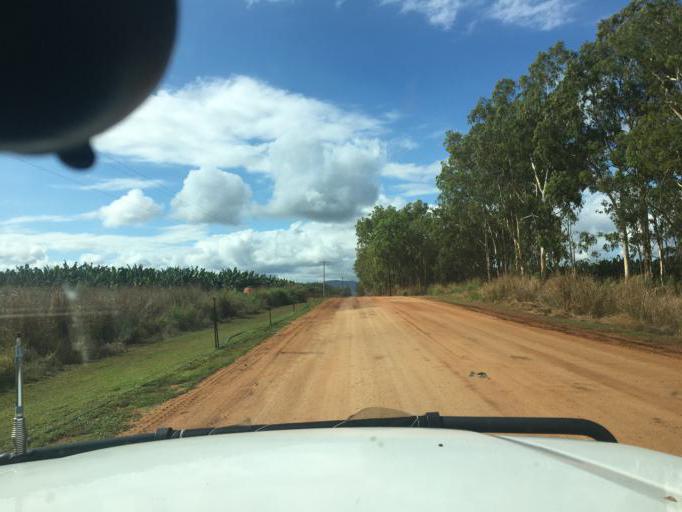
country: AU
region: Queensland
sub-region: Tablelands
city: Mareeba
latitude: -17.0940
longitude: 145.4123
